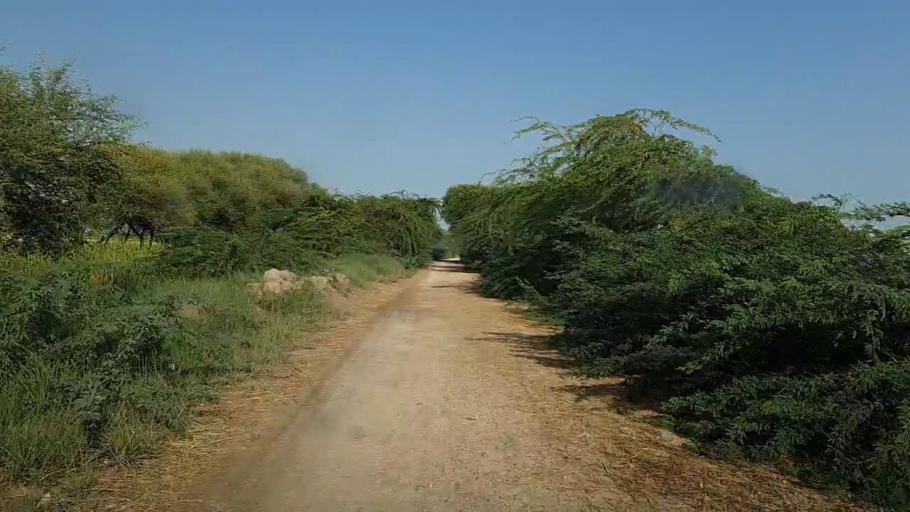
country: PK
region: Sindh
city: Bulri
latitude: 24.7743
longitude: 68.4306
